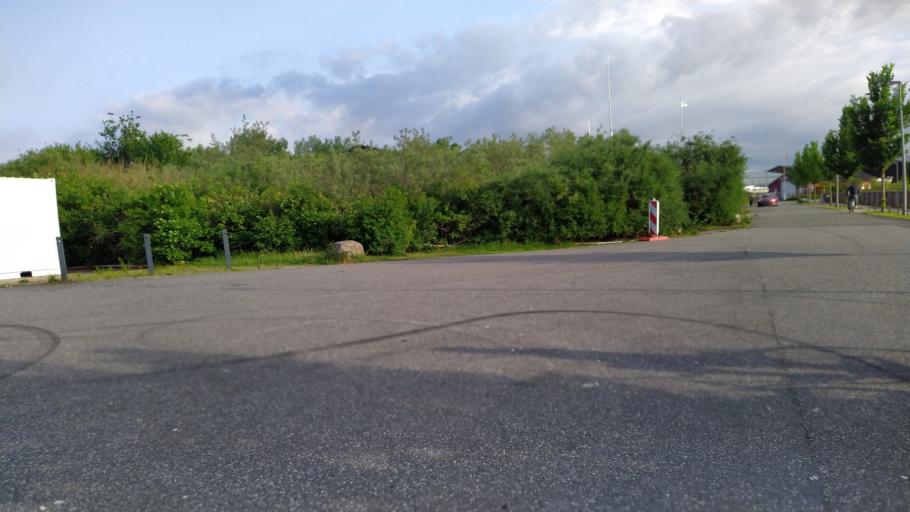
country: DE
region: Hamburg
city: Altona
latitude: 53.5421
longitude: 9.8575
